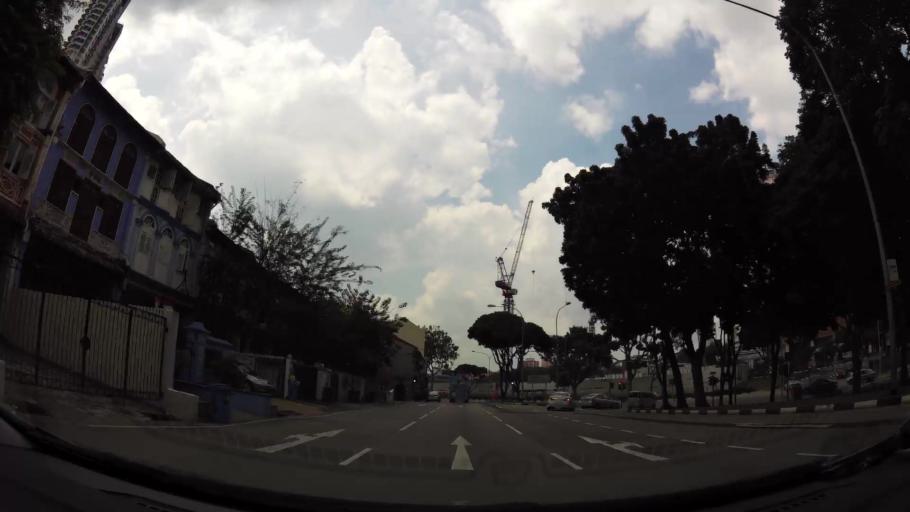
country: SG
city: Singapore
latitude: 1.2773
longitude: 103.8374
